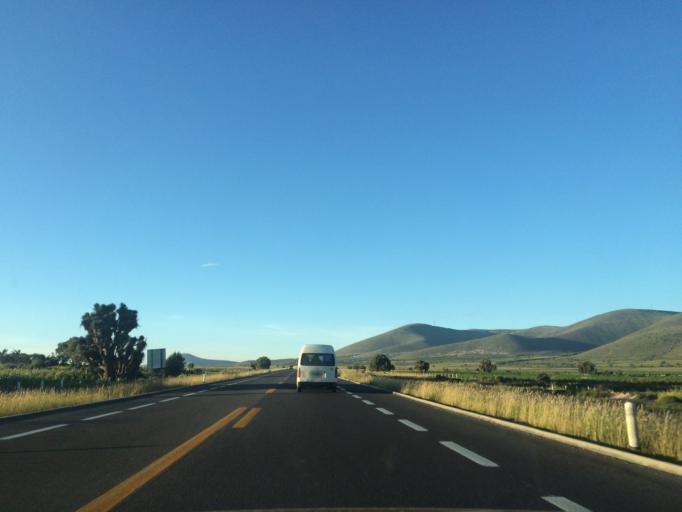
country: MX
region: Puebla
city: Cuacnopalan
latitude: 18.7586
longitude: -97.4820
